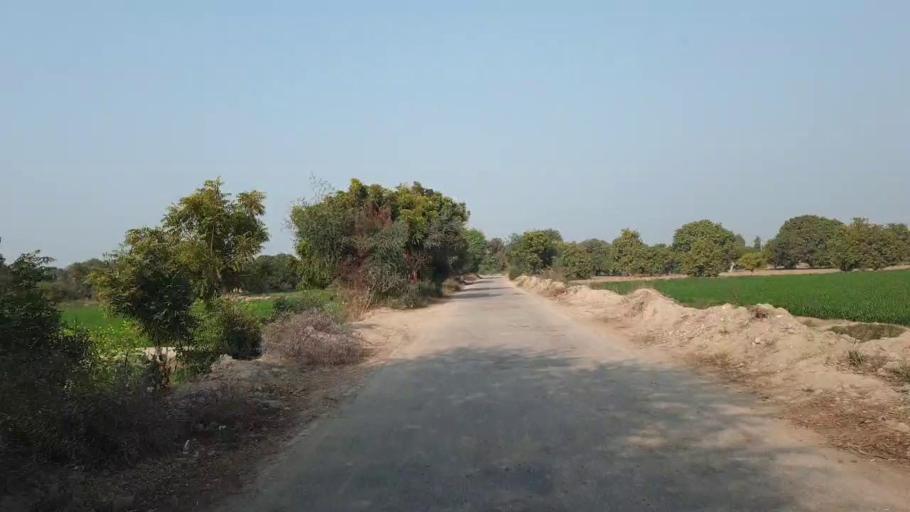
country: PK
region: Sindh
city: Hala
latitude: 25.8423
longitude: 68.4613
